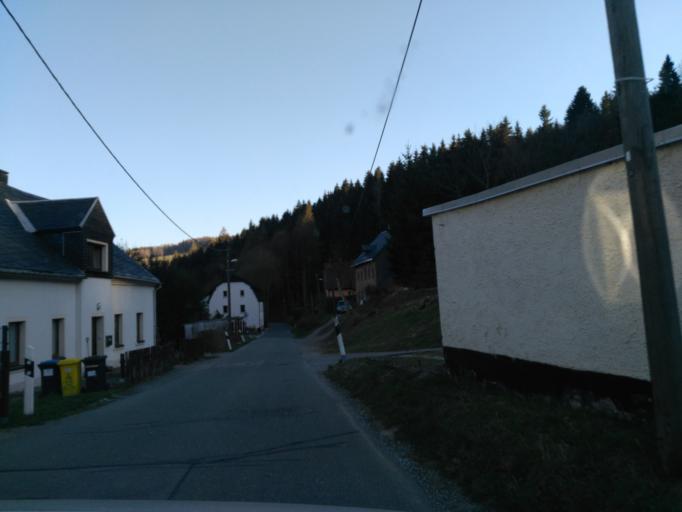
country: DE
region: Saxony
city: Barenstein
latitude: 50.5158
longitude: 13.0385
